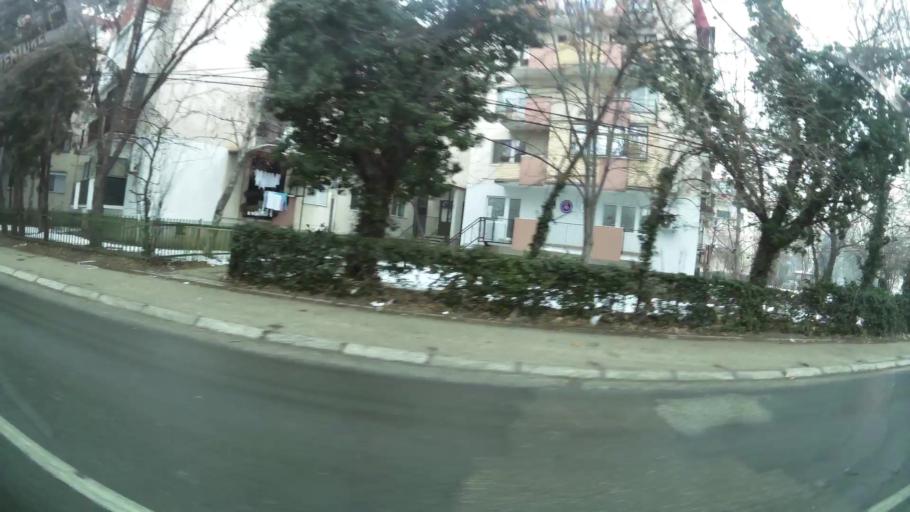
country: MK
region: Saraj
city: Saraj
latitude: 42.0212
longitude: 21.3517
